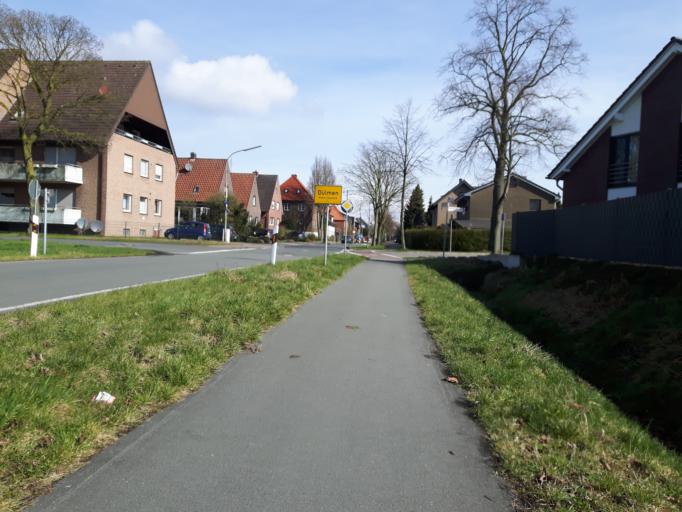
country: DE
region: North Rhine-Westphalia
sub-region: Regierungsbezirk Munster
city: Dulmen
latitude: 51.8186
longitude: 7.2727
